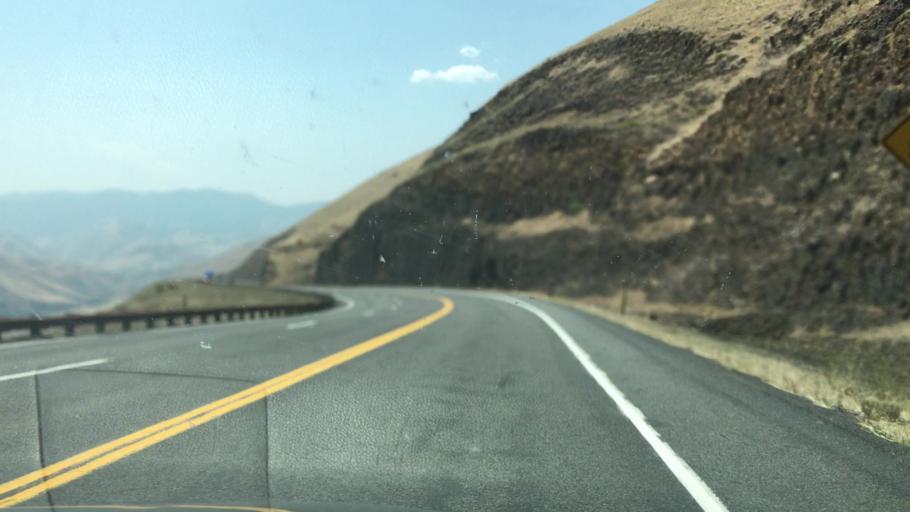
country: US
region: Idaho
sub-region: Idaho County
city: Grangeville
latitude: 45.8153
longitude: -116.2765
